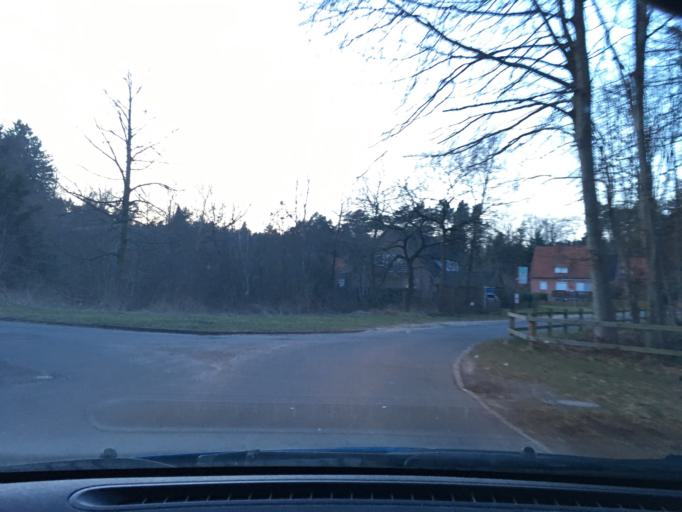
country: DE
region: Lower Saxony
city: Egestorf
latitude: 53.1806
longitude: 10.0636
